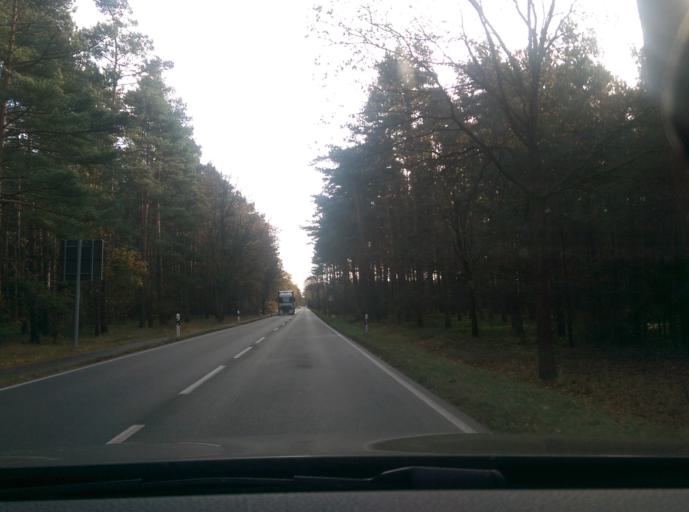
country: DE
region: Lower Saxony
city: Hambuhren
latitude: 52.6633
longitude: 9.9806
